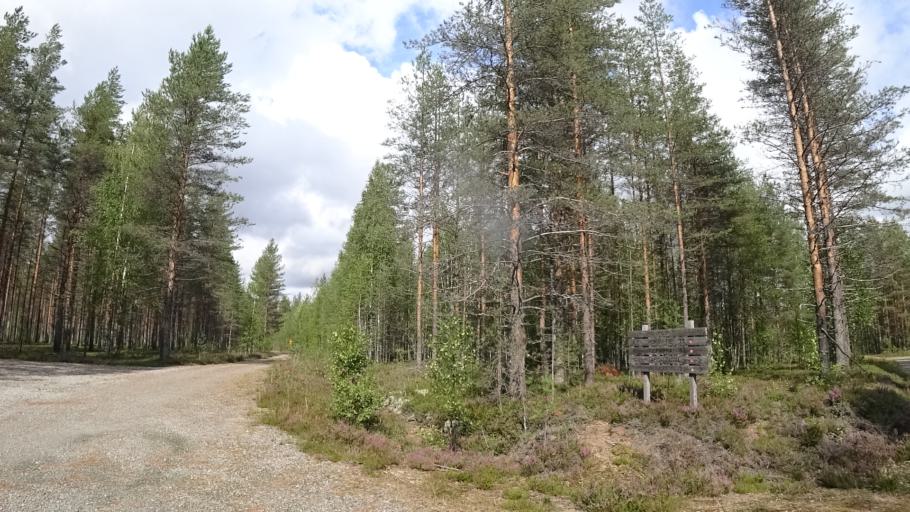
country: FI
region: North Karelia
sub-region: Joensuu
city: Ilomantsi
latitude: 62.9389
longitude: 31.4351
